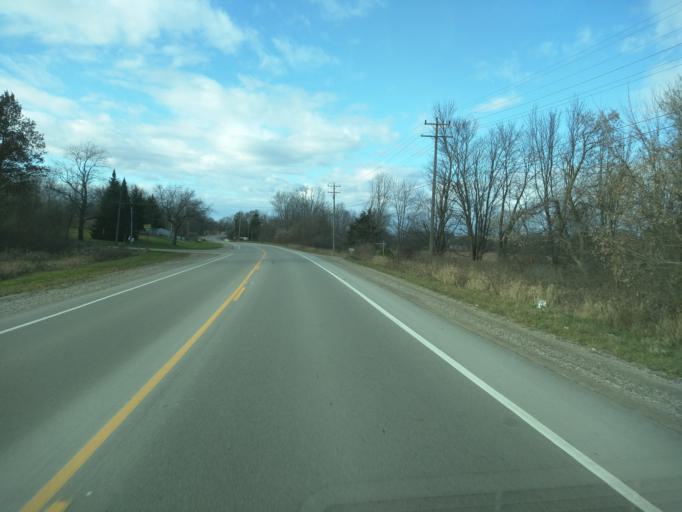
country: US
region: Michigan
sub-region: Ingham County
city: Webberville
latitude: 42.6680
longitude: -84.1369
